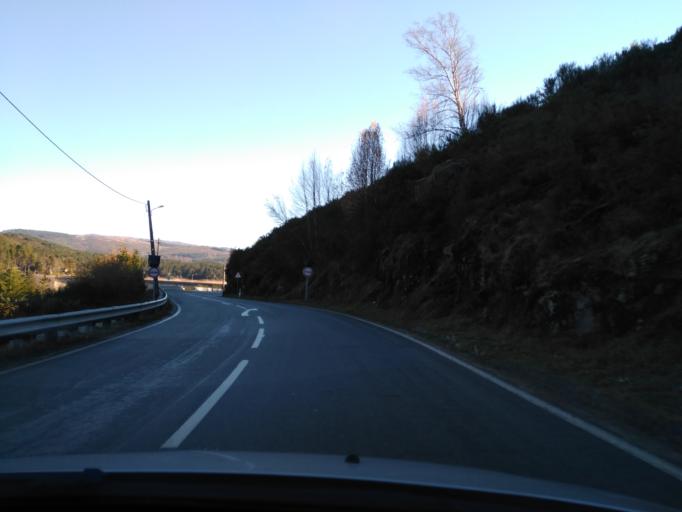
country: PT
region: Braga
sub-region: Vieira do Minho
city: Vieira do Minho
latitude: 41.6795
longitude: -7.9891
